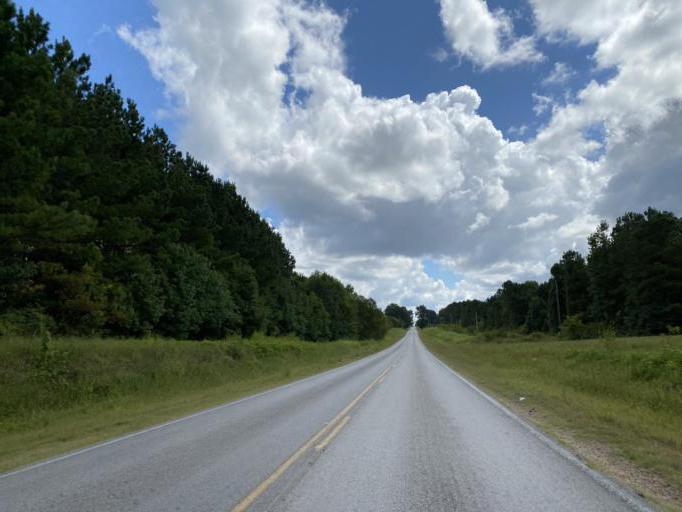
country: US
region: Mississippi
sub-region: Panola County
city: Como
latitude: 34.5105
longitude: -90.0229
